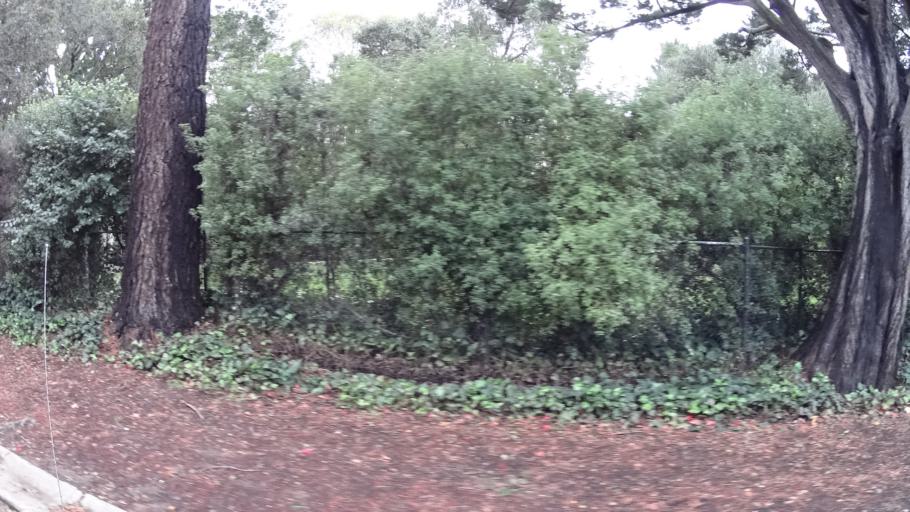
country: US
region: California
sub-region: San Mateo County
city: Burlingame
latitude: 37.5670
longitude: -122.3515
